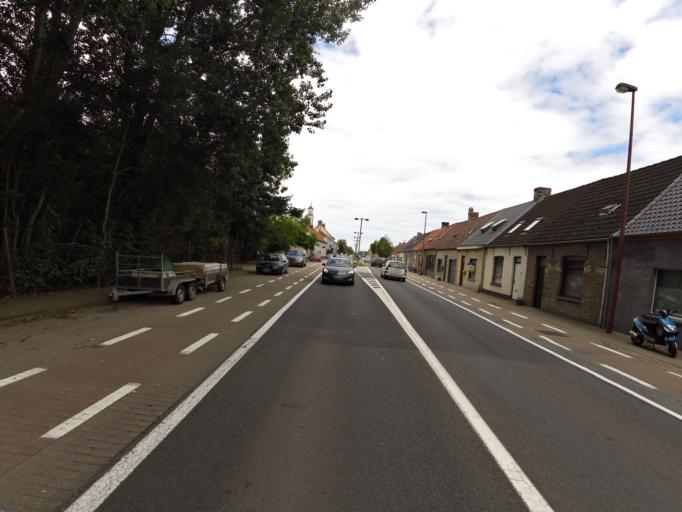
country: BE
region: Flanders
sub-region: Provincie West-Vlaanderen
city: Gistel
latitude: 51.1304
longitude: 2.9850
